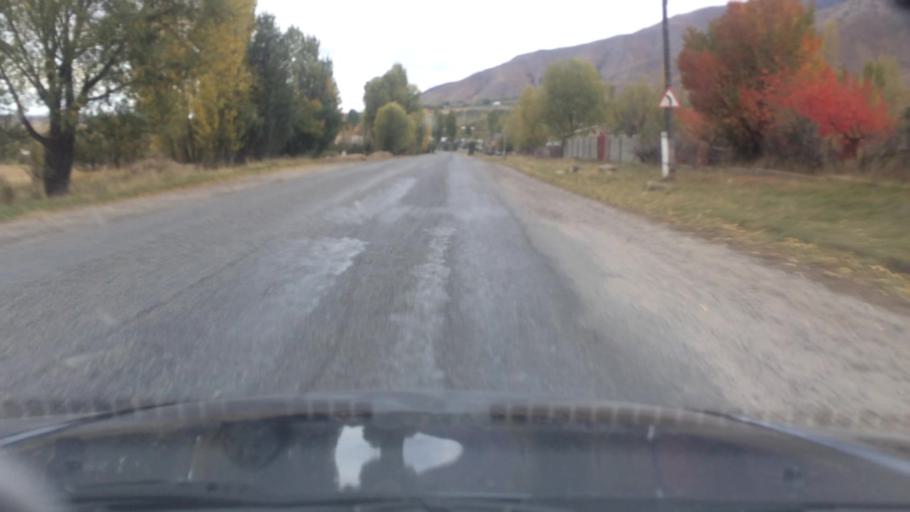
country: KG
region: Ysyk-Koel
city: Tyup
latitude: 42.7475
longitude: 78.0965
